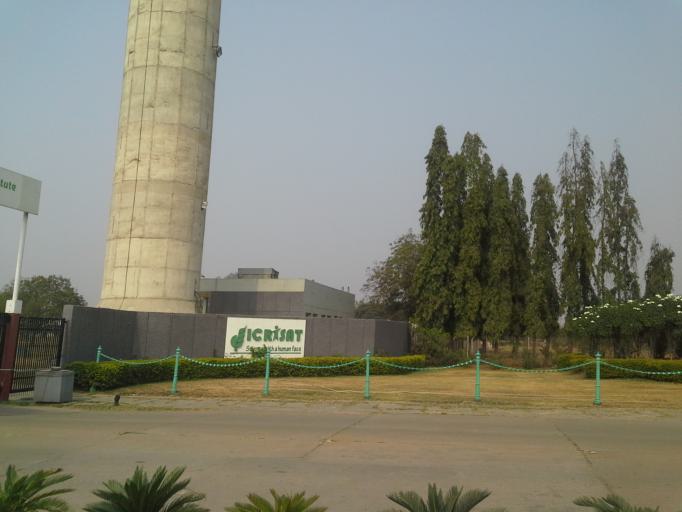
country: IN
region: Telangana
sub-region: Medak
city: Patancheru
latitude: 17.5179
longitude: 78.2791
